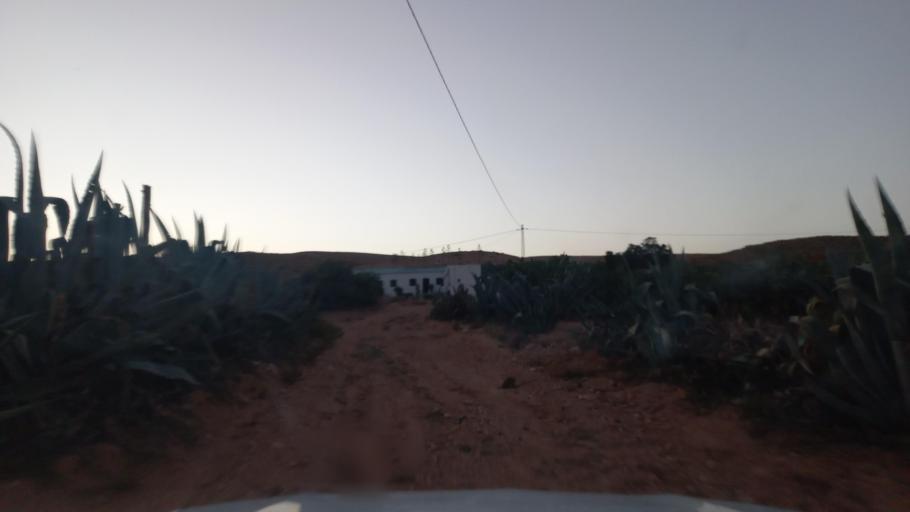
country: TN
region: Al Qasrayn
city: Sbiba
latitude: 35.3783
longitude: 9.0106
